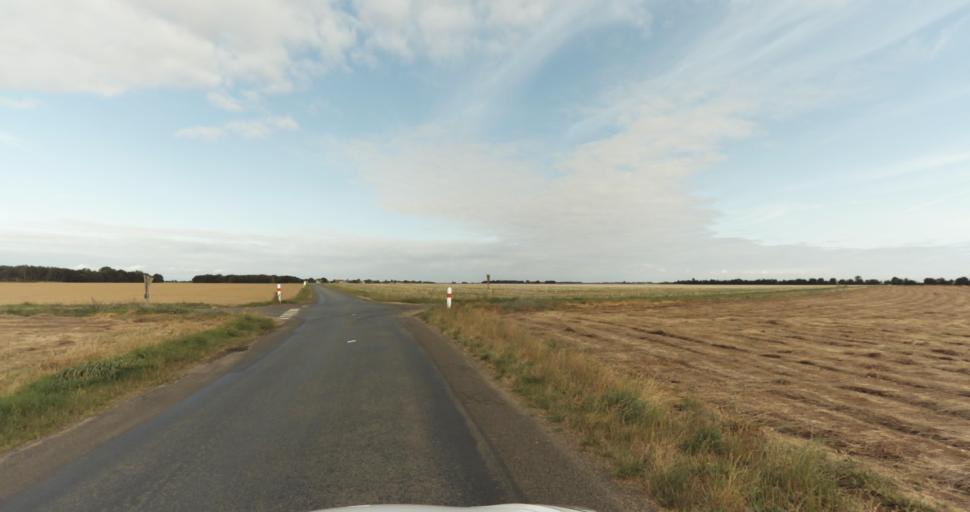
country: FR
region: Haute-Normandie
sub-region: Departement de l'Eure
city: La Madeleine-de-Nonancourt
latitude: 48.8676
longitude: 1.2308
